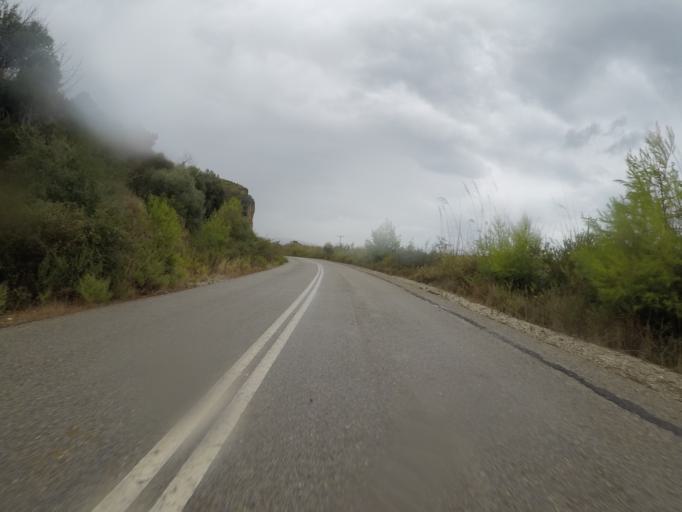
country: GR
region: West Greece
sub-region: Nomos Ileias
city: Zacharo
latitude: 37.5246
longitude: 21.5948
